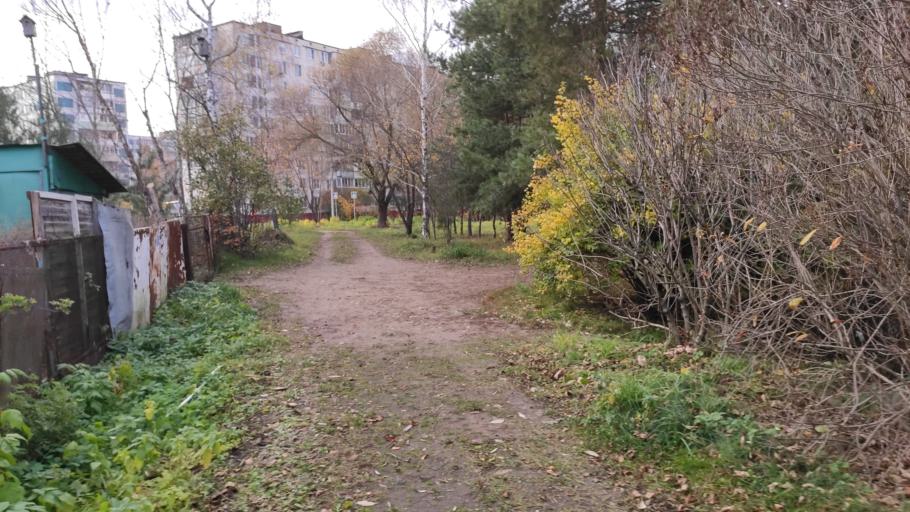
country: RU
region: Moskovskaya
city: Noginsk
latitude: 55.8659
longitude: 38.4502
